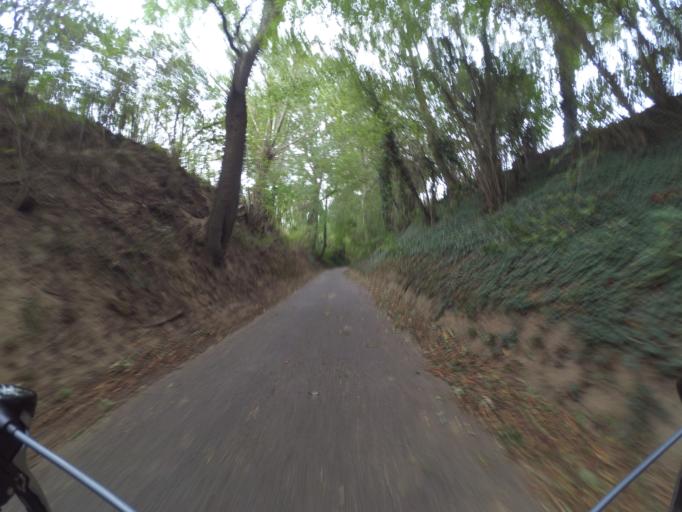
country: NL
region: Limburg
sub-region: Gemeente Maastricht
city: Heer
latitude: 50.8483
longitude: 5.7512
